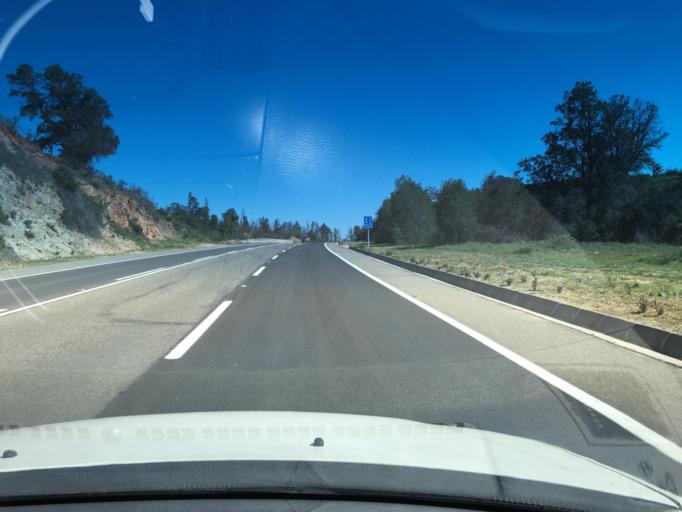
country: CL
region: Valparaiso
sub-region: San Antonio Province
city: El Tabo
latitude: -33.4055
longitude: -71.5044
